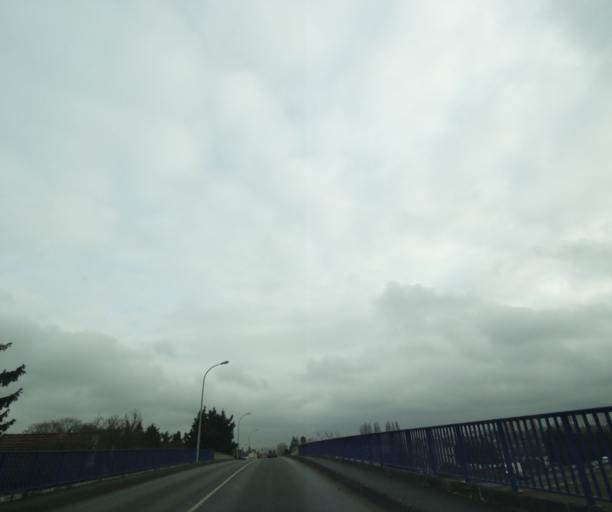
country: FR
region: Ile-de-France
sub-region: Departement de l'Essonne
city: Champlan
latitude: 48.7020
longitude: 2.2847
